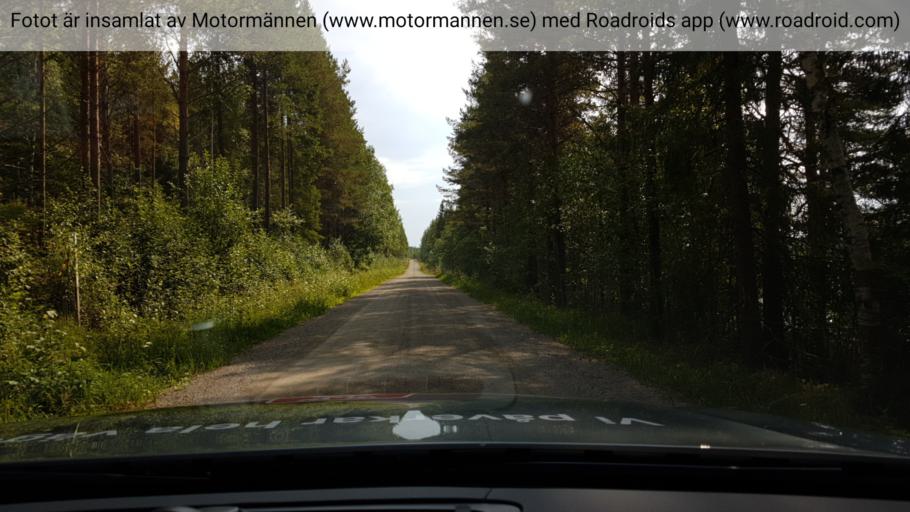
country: SE
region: Jaemtland
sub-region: OEstersunds Kommun
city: Brunflo
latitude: 63.0249
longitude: 15.0904
